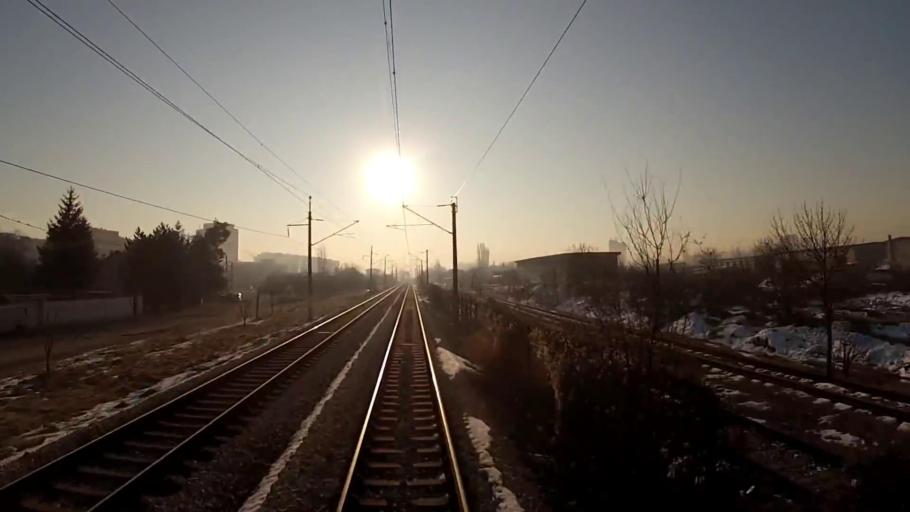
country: BG
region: Sofia-Capital
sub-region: Stolichna Obshtina
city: Sofia
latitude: 42.7324
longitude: 23.2722
